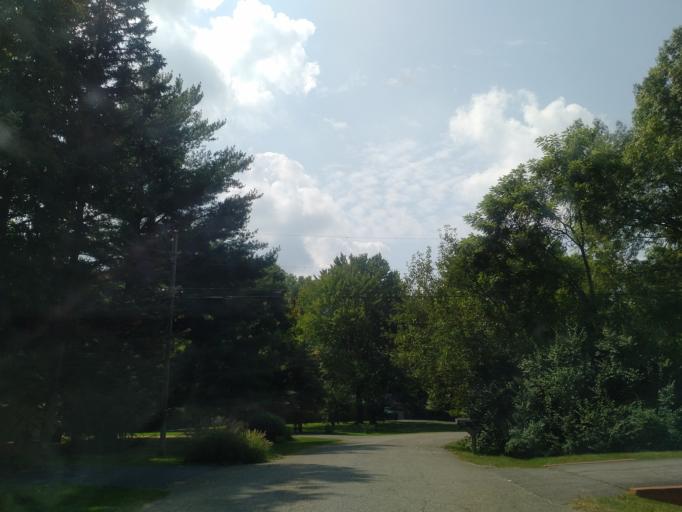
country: US
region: Indiana
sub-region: Marion County
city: Meridian Hills
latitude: 39.9156
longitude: -86.1276
